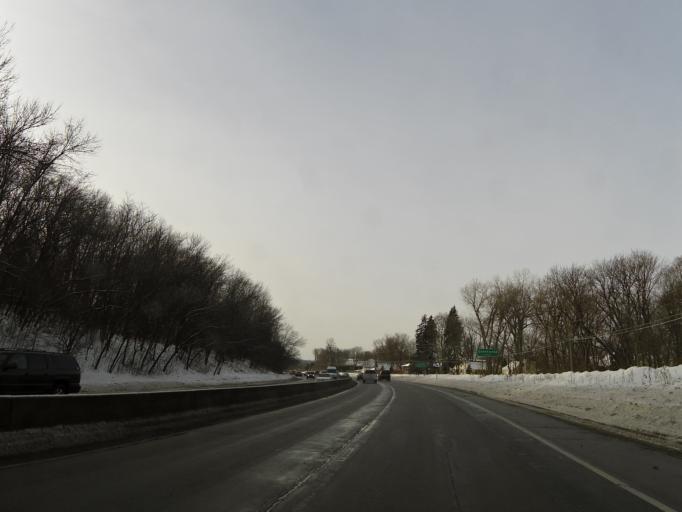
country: US
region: Minnesota
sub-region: Hennepin County
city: Excelsior
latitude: 44.9054
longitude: -93.5445
